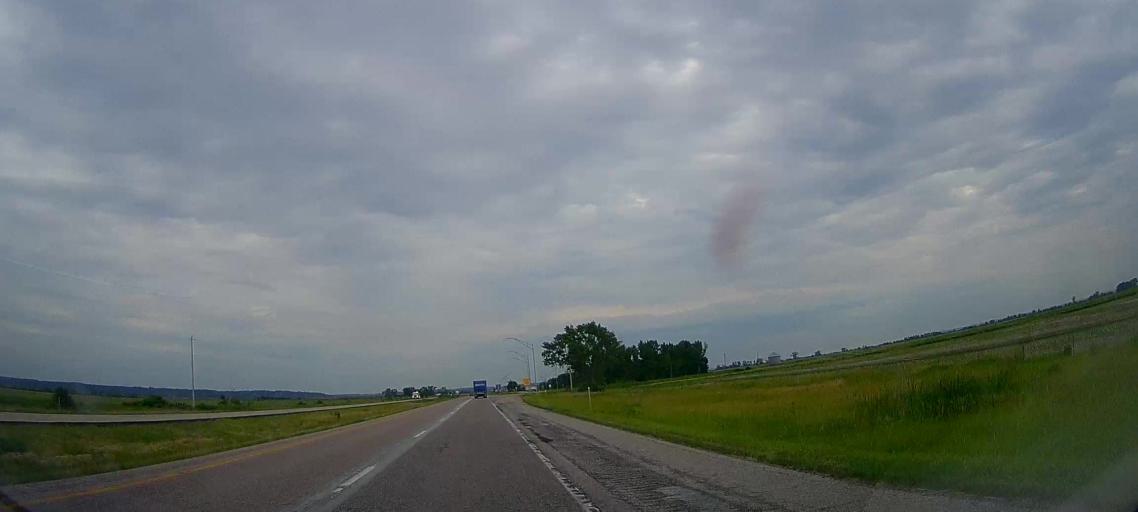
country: US
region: Iowa
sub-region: Harrison County
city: Missouri Valley
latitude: 41.5954
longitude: -95.9568
